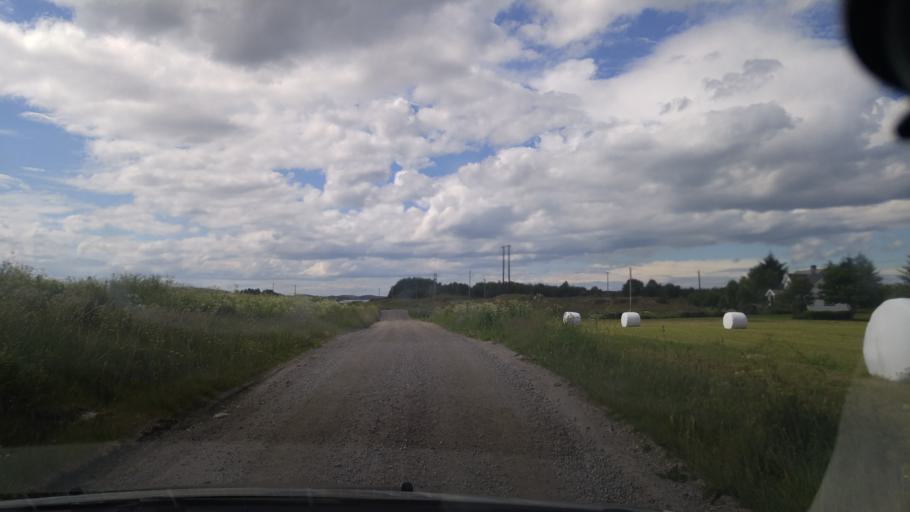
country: NO
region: Nord-Trondelag
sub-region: Vikna
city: Rorvik
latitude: 64.9029
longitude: 11.1133
